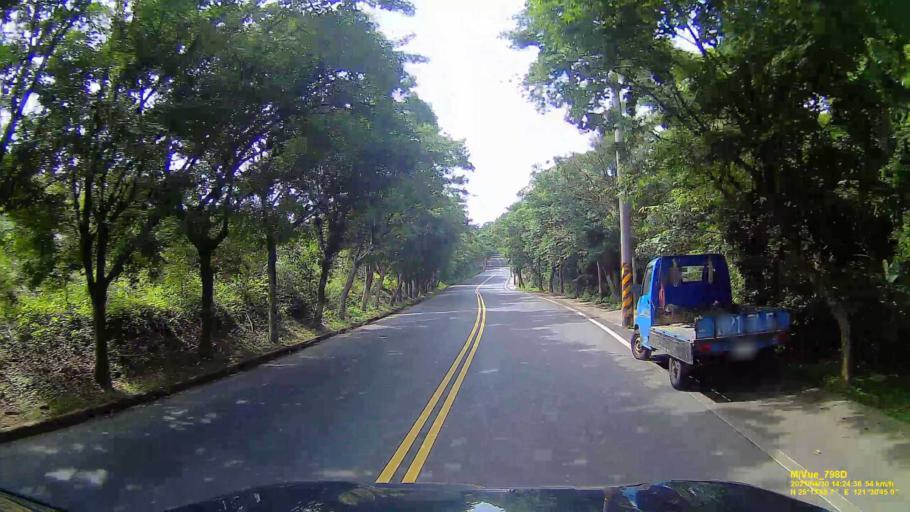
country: TW
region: Taipei
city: Taipei
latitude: 25.2305
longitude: 121.5123
